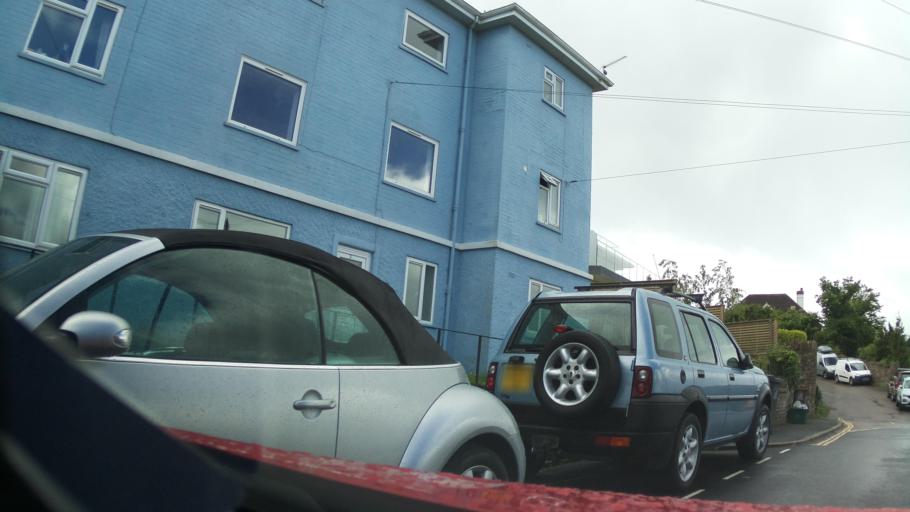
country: GB
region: England
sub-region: Devon
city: Dartmouth
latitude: 50.3490
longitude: -3.5685
